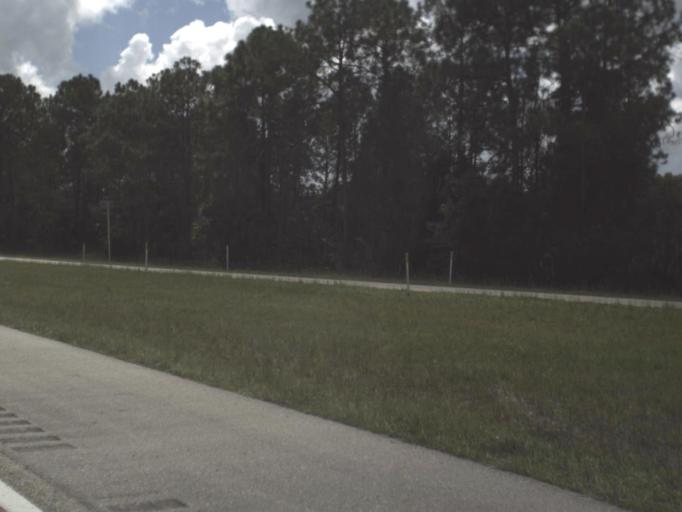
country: US
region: Florida
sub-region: Collier County
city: Golden Gate
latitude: 26.1591
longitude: -81.6824
